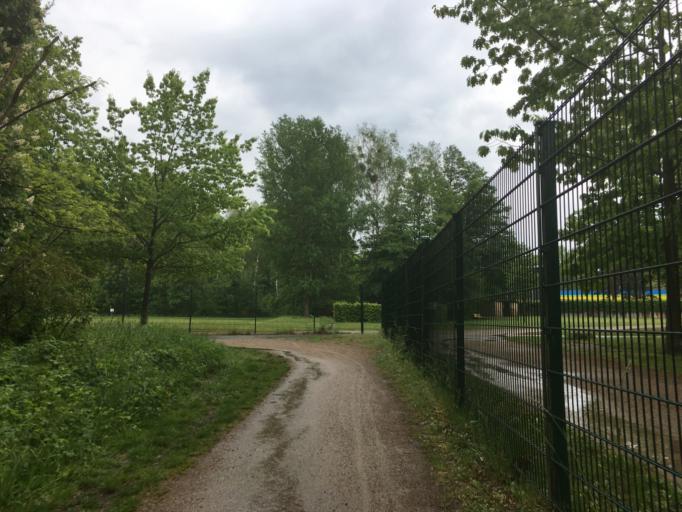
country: DE
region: Brandenburg
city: Eberswalde
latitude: 52.8440
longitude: 13.7713
